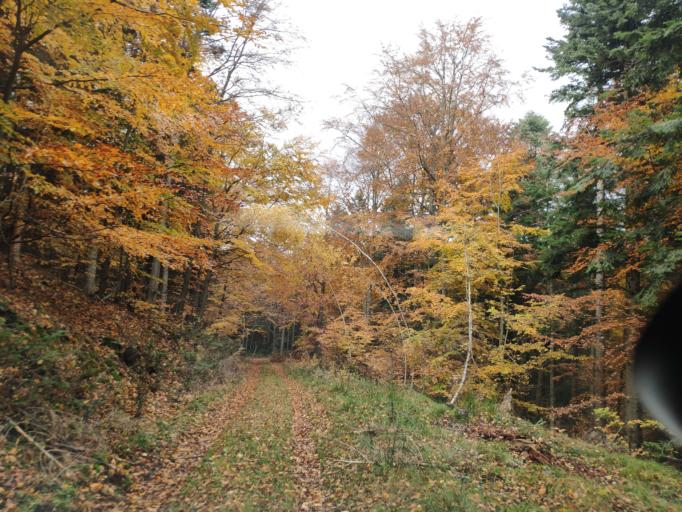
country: SK
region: Kosicky
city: Medzev
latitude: 48.7561
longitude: 20.9818
